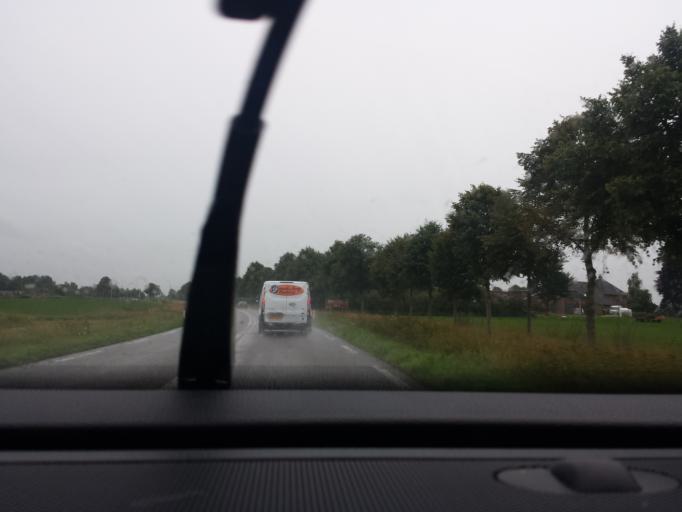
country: NL
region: Gelderland
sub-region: Gemeente Bronckhorst
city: Hengelo
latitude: 52.0214
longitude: 6.2989
